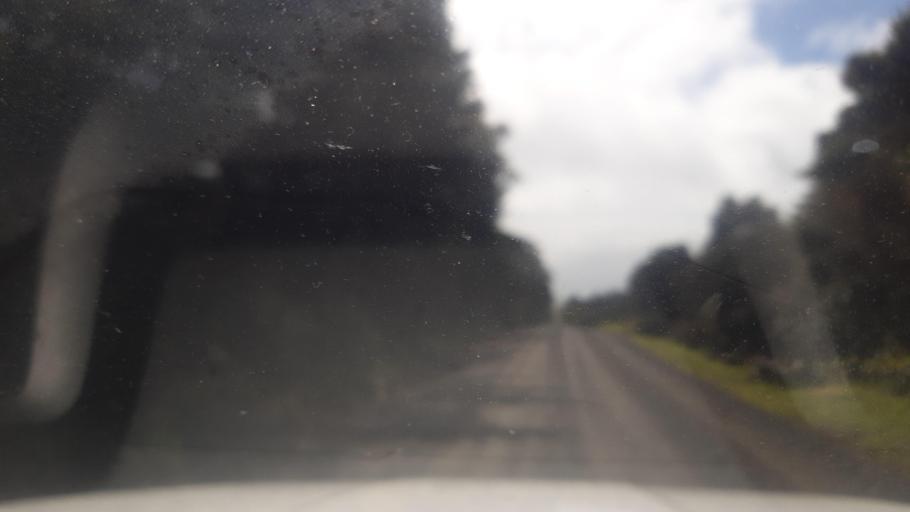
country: NZ
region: Northland
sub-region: Far North District
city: Kaitaia
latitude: -34.7427
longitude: 173.1089
